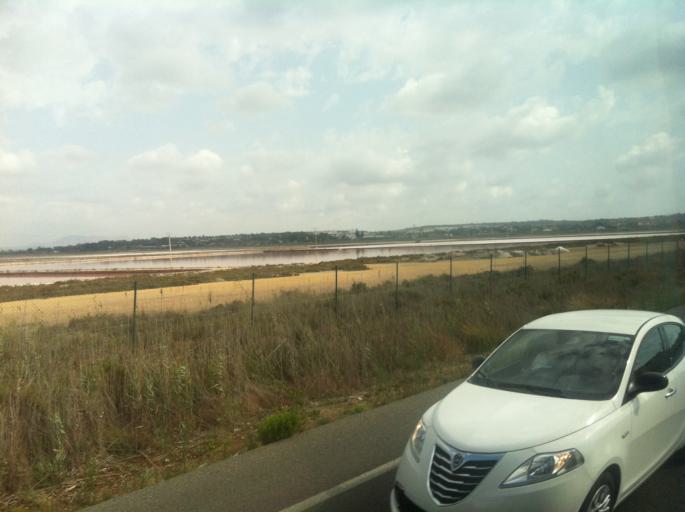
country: ES
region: Valencia
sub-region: Provincia de Alicante
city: Santa Pola
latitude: 38.1940
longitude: -0.5868
